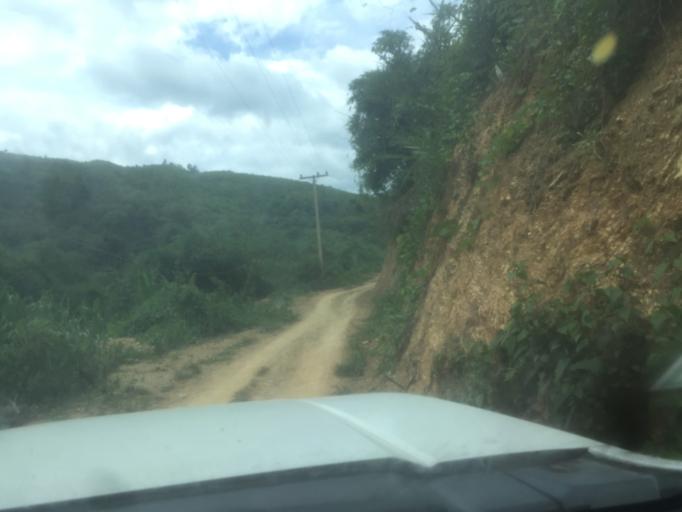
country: LA
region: Phongsali
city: Khoa
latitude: 20.9108
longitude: 102.5600
